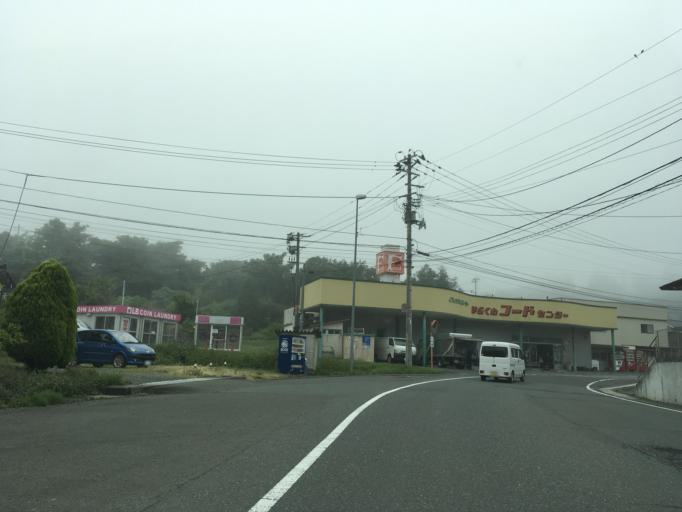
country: JP
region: Iwate
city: Ofunato
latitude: 38.9041
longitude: 141.6490
